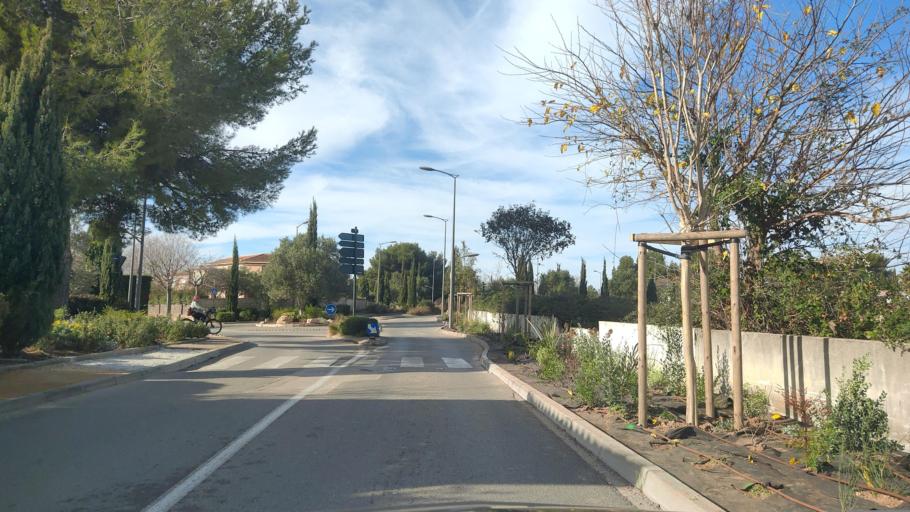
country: FR
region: Provence-Alpes-Cote d'Azur
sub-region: Departement du Var
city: Sanary-sur-Mer
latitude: 43.1279
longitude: 5.8072
